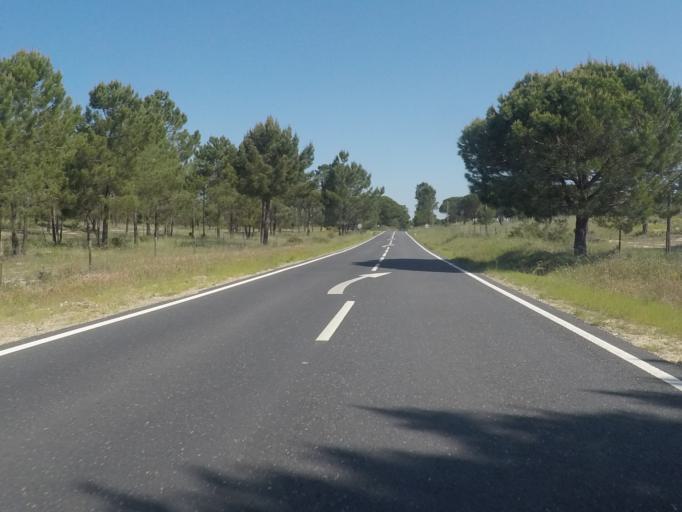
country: PT
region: Setubal
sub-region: Grandola
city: Grandola
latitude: 38.2834
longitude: -8.7260
